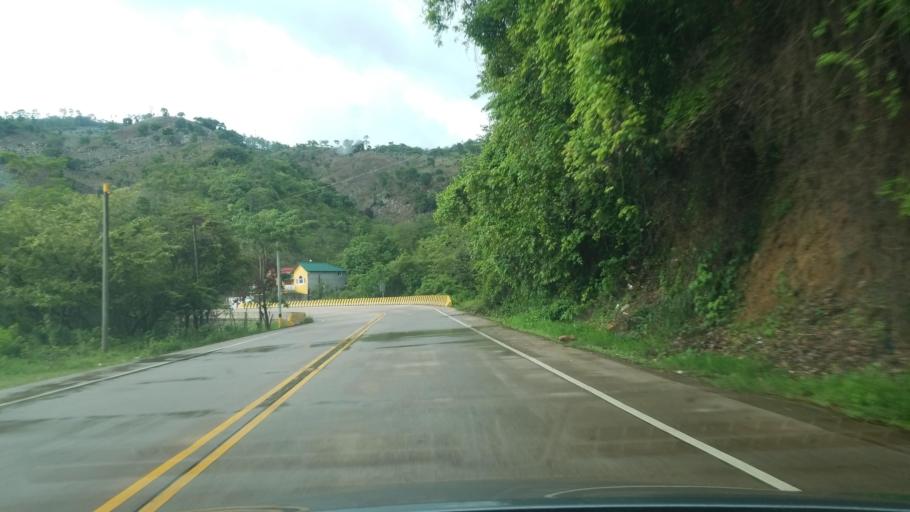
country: HN
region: Copan
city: Copan
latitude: 14.8444
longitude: -89.1893
